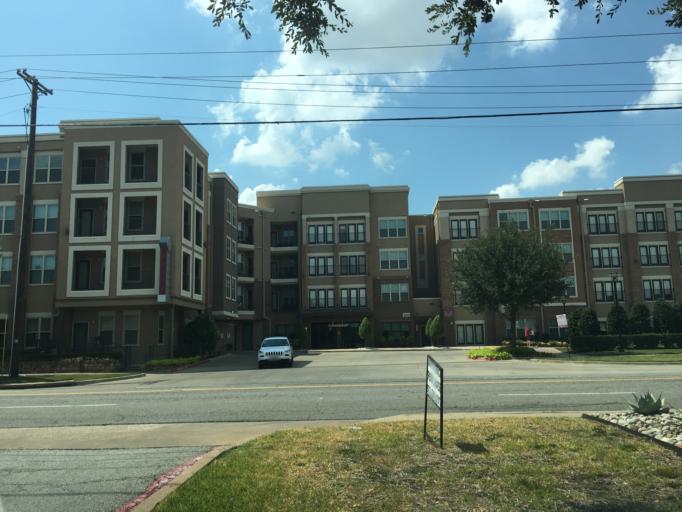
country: US
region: Texas
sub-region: Dallas County
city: Addison
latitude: 32.9688
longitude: -96.8288
